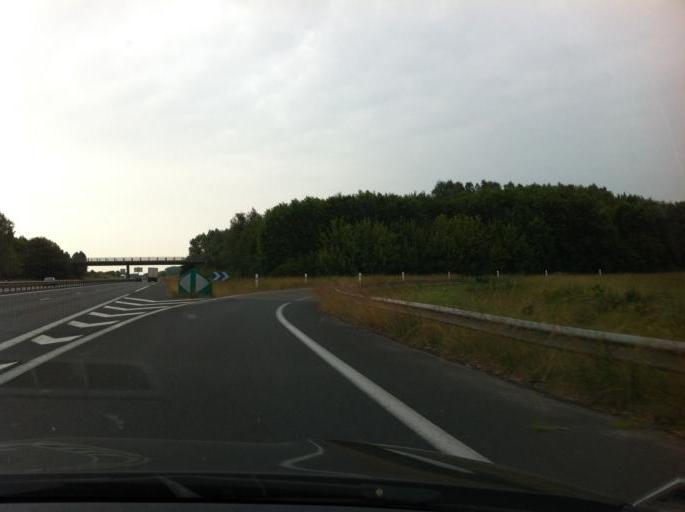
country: FR
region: Ile-de-France
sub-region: Departement de Seine-et-Marne
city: Moissy-Cramayel
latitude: 48.6117
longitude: 2.6324
